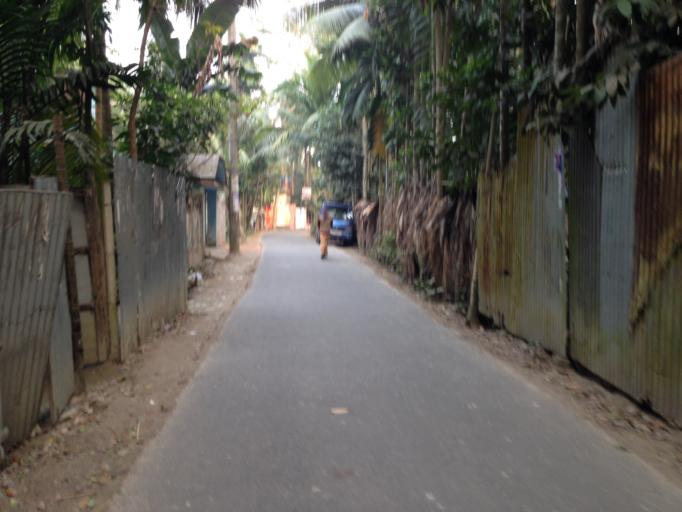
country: BD
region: Chittagong
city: Lakshmipur
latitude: 22.9203
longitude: 90.8394
